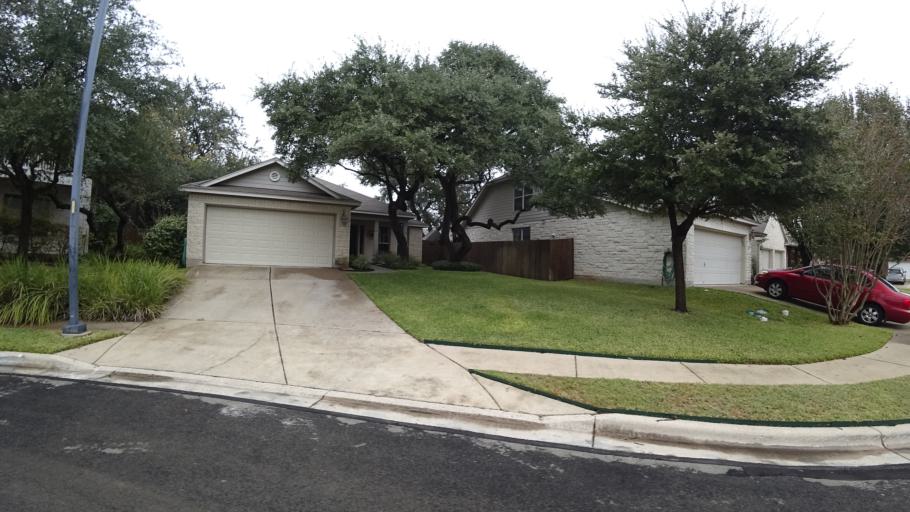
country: US
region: Texas
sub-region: Travis County
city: Shady Hollow
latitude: 30.1898
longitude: -97.8683
